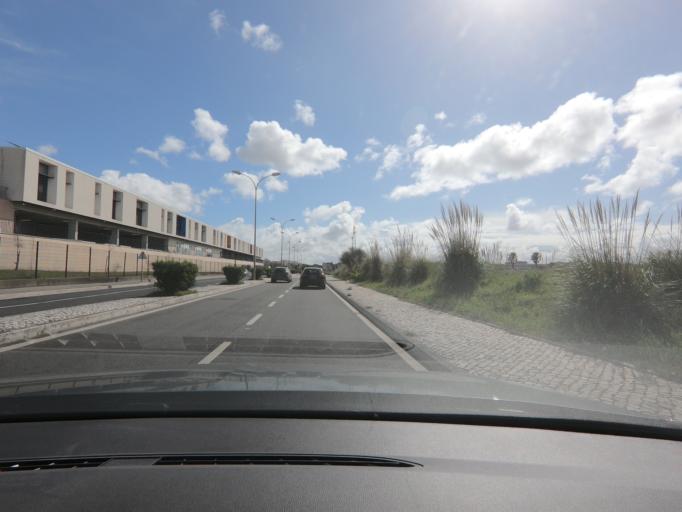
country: PT
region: Lisbon
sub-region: Oeiras
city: Porto Salvo
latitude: 38.7140
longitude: -9.3066
